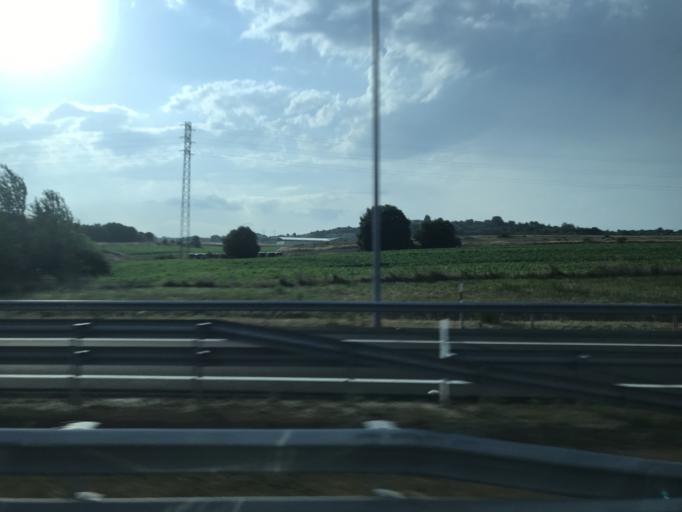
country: ES
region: Basque Country
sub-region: Provincia de Alava
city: Gasteiz / Vitoria
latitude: 42.9134
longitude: -2.7001
